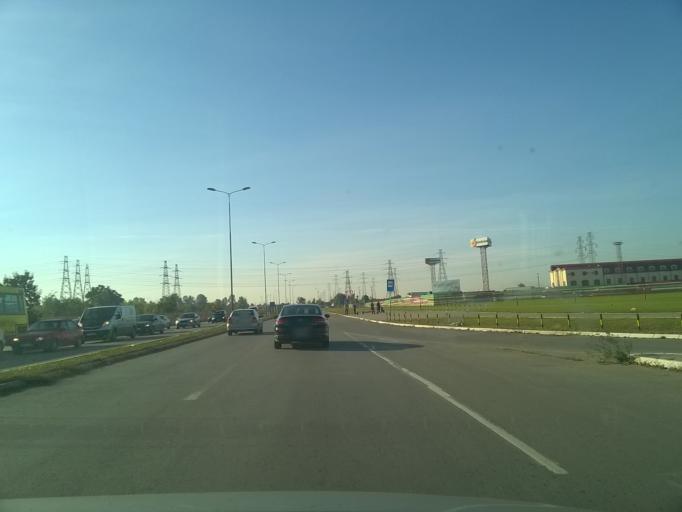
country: RS
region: Central Serbia
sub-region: Belgrade
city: Zemun
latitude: 44.8263
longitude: 20.3620
